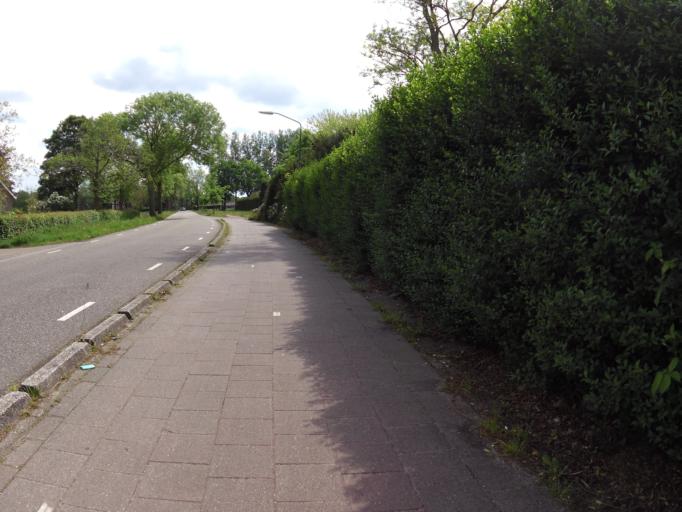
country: NL
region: North Brabant
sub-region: Gemeente Boxtel
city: Boxtel
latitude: 51.6041
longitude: 5.3450
